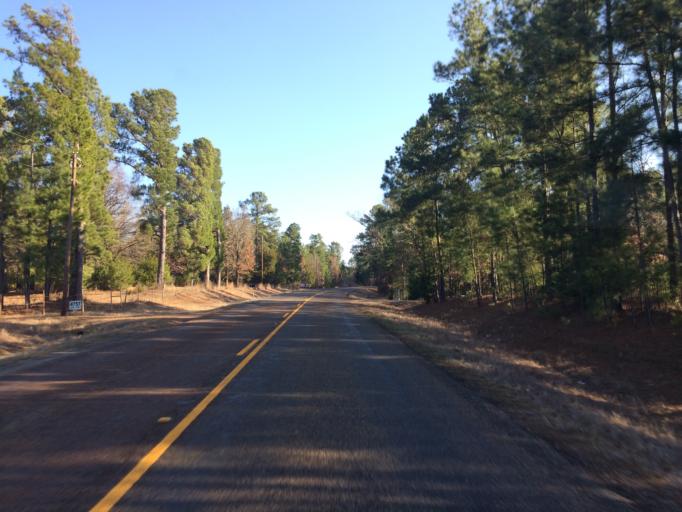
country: US
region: Texas
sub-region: Wood County
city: Mineola
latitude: 32.6847
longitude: -95.3377
